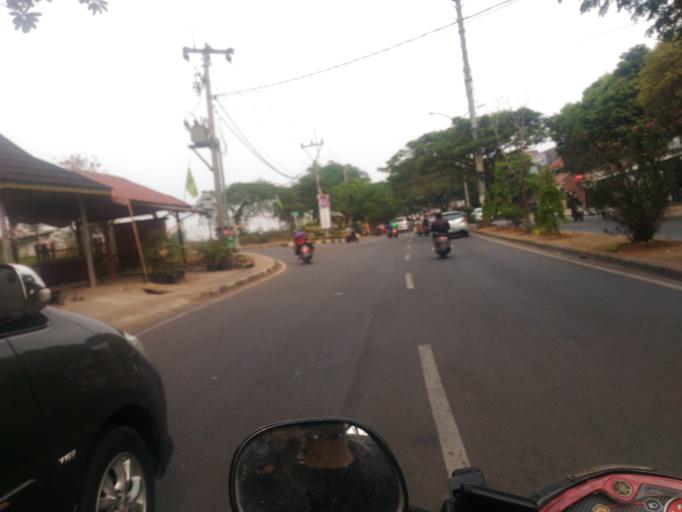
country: ID
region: West Java
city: Depok
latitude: -6.3800
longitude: 106.8541
